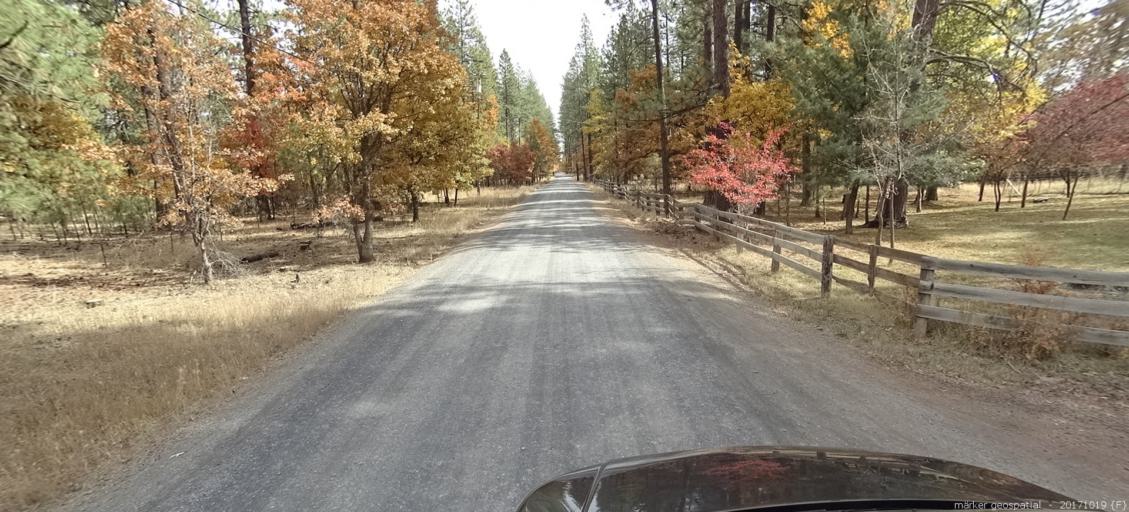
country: US
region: California
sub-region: Shasta County
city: Burney
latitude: 41.0799
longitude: -121.5329
